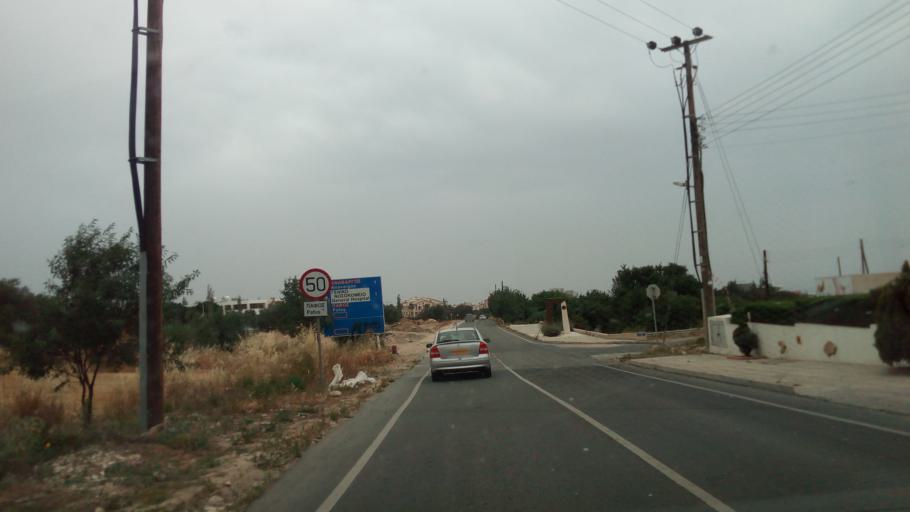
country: CY
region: Pafos
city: Mesogi
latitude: 34.8021
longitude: 32.4495
